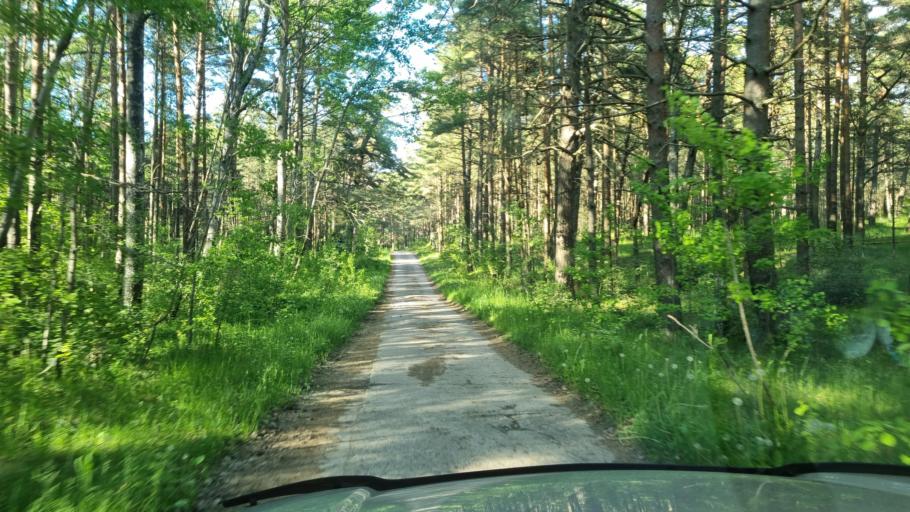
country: LV
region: Ventspils
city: Ventspils
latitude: 57.3681
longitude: 21.5189
